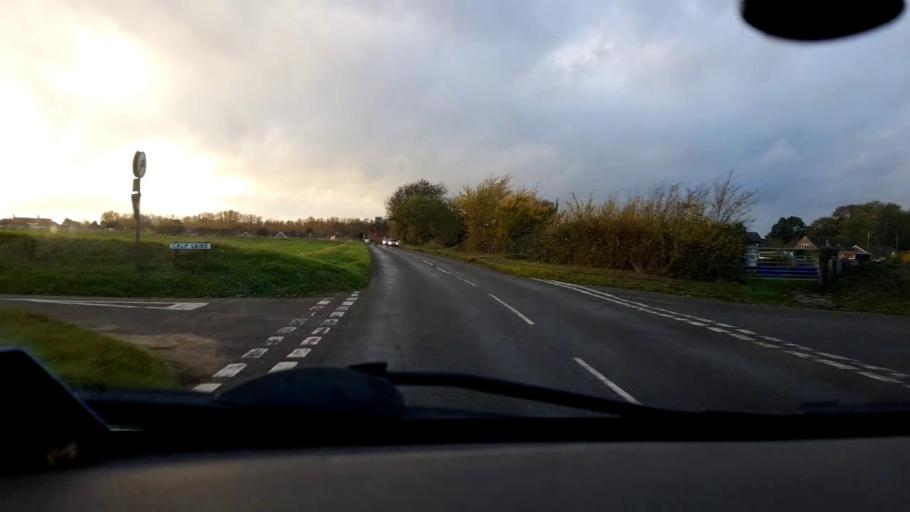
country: GB
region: England
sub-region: Norfolk
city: Spixworth
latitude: 52.6884
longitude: 1.2860
